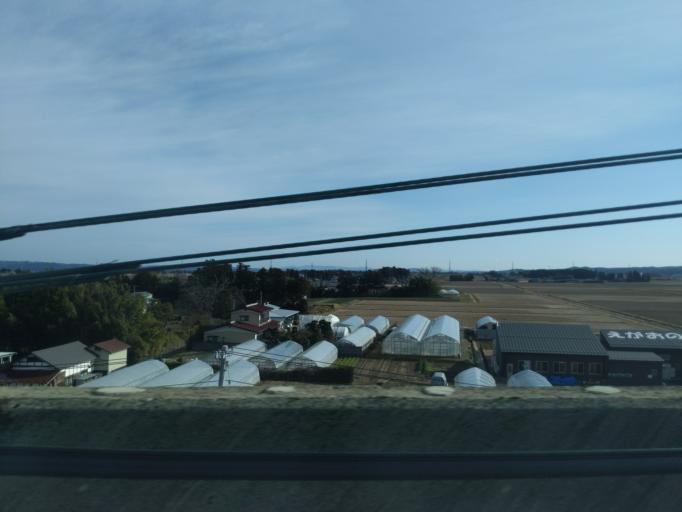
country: JP
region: Miyagi
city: Furukawa
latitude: 38.5544
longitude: 140.9635
